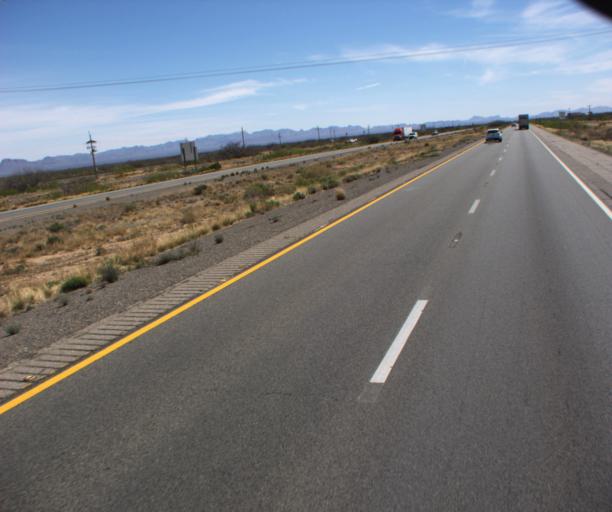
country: US
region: Arizona
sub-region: Cochise County
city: Willcox
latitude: 32.3152
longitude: -109.4332
